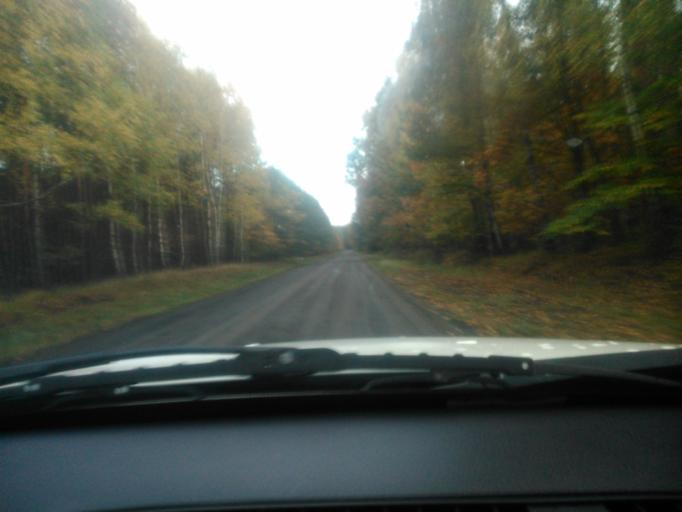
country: PL
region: Kujawsko-Pomorskie
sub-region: Powiat golubsko-dobrzynski
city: Golub-Dobrzyn
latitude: 53.1573
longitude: 19.1286
